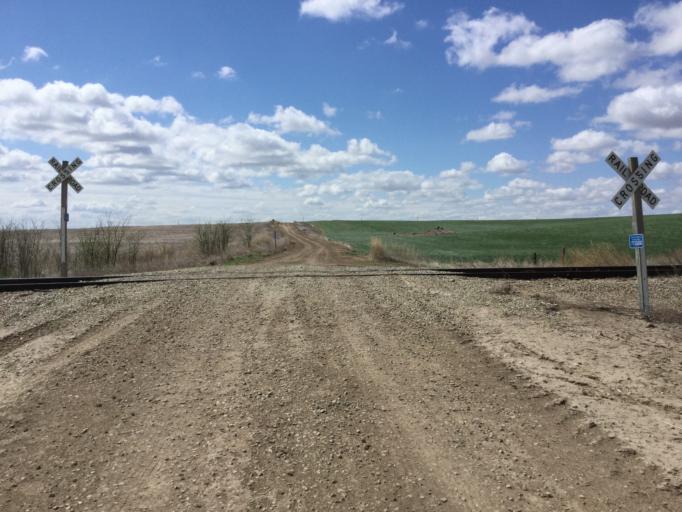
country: US
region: Kansas
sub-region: Phillips County
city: Phillipsburg
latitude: 39.7624
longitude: -99.1786
